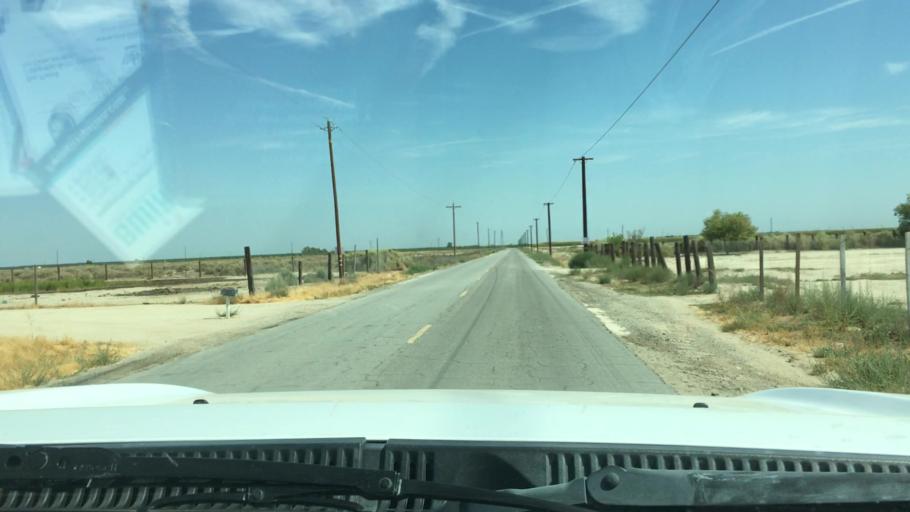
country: US
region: California
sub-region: Kern County
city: Buttonwillow
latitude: 35.4305
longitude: -119.3761
